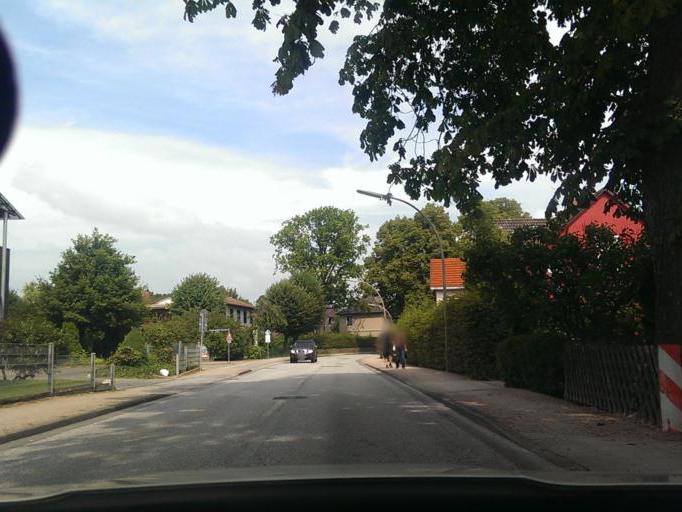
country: DE
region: Hamburg
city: Duvenstedt
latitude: 53.7056
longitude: 10.1029
